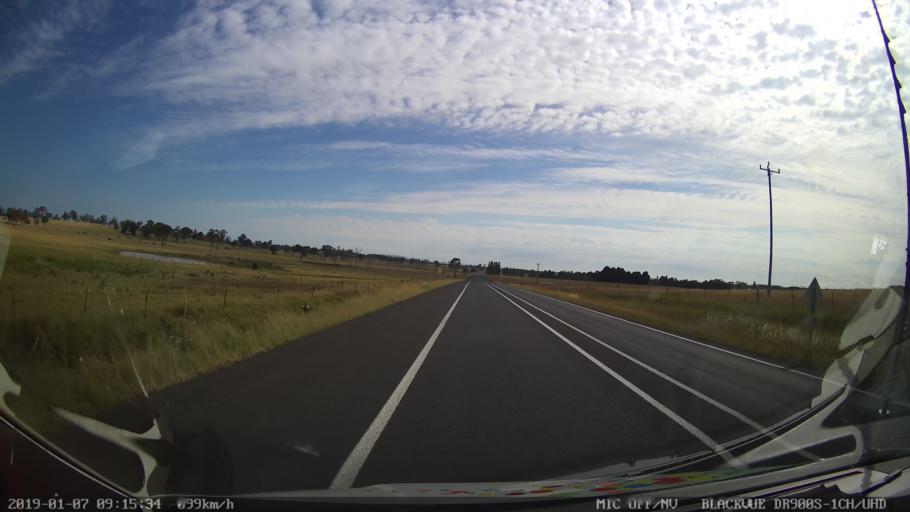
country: AU
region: New South Wales
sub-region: Armidale Dumaresq
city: Armidale
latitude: -30.6125
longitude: 151.5364
